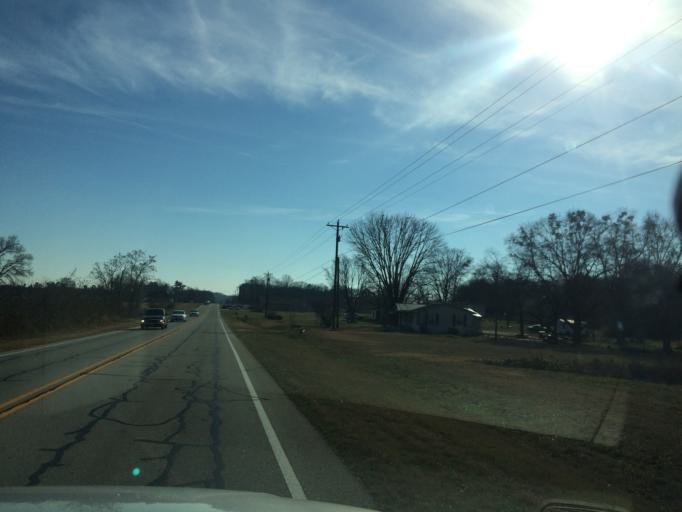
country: US
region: Georgia
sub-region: Franklin County
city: Lavonia
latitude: 34.4235
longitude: -83.0266
